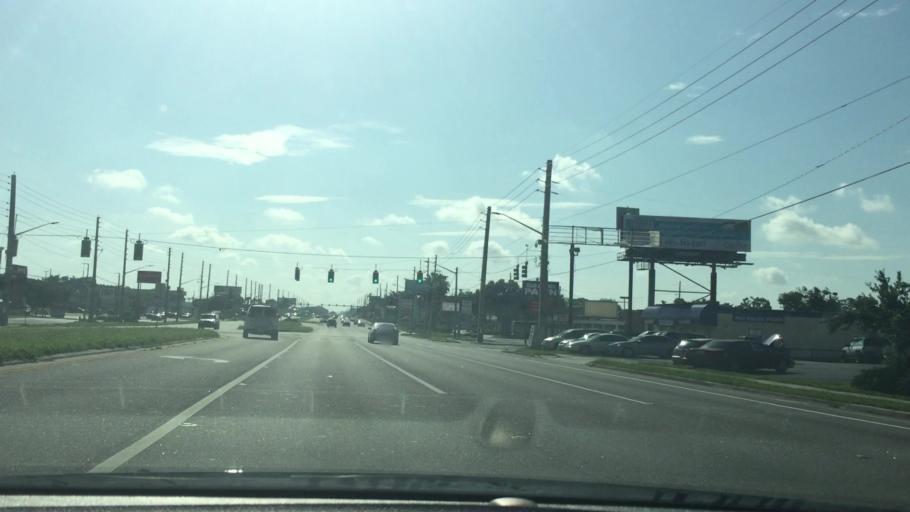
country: US
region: Florida
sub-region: Orange County
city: Pine Hills
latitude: 28.5524
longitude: -81.4521
